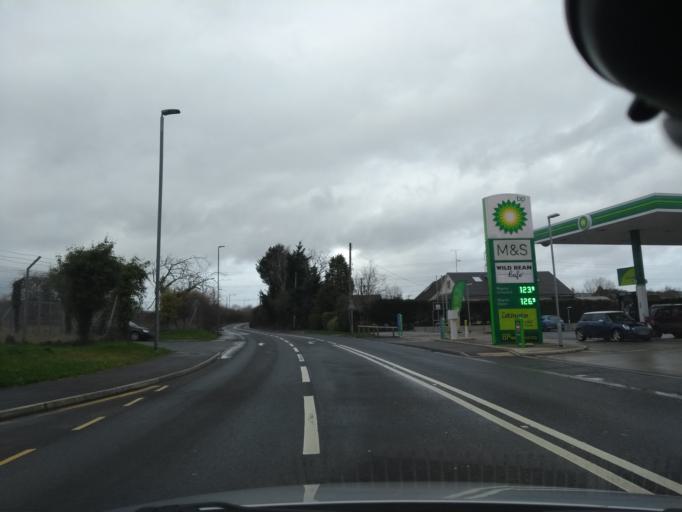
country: GB
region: England
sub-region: Somerset
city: Taunton
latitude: 51.0315
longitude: -3.1365
